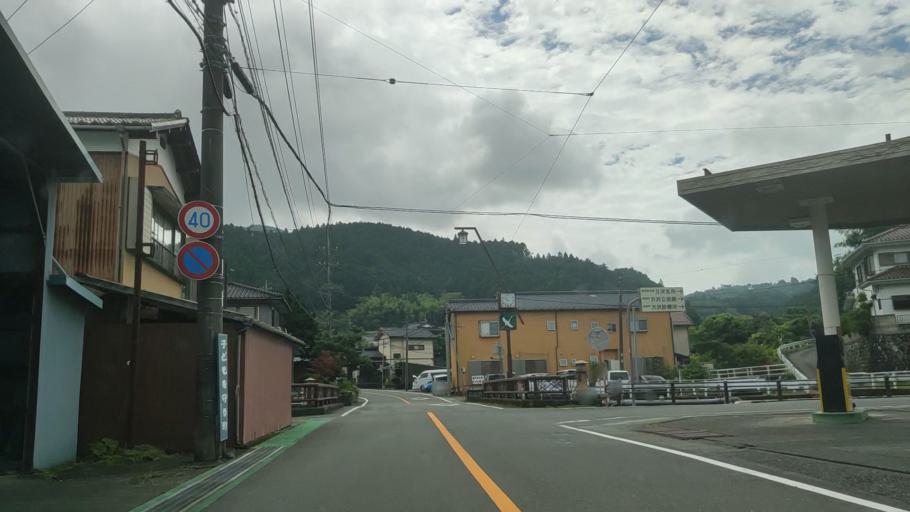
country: JP
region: Shizuoka
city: Fujinomiya
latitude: 35.2193
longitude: 138.5161
